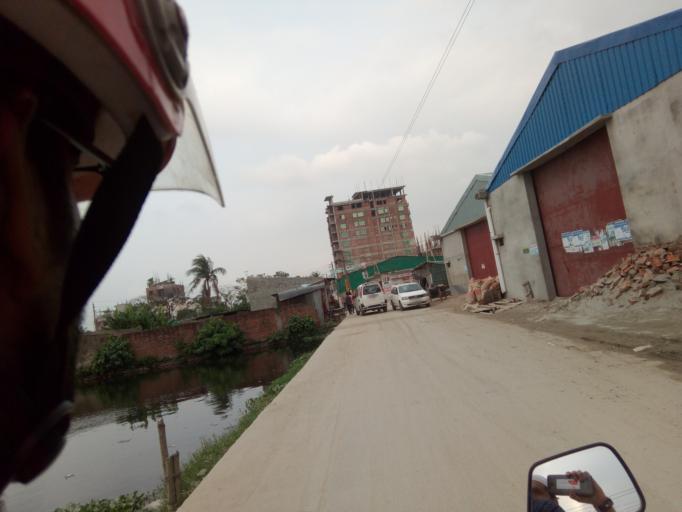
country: BD
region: Dhaka
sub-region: Dhaka
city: Dhaka
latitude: 23.7018
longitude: 90.4745
